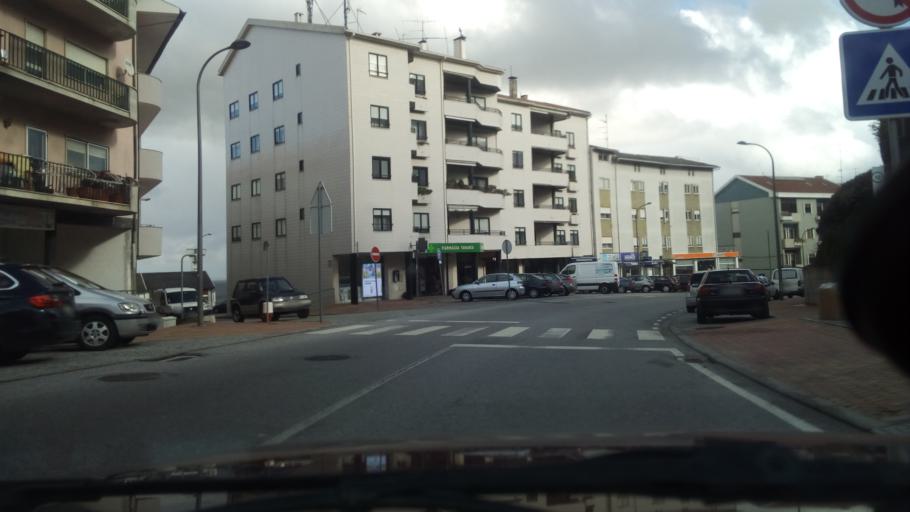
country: PT
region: Guarda
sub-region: Guarda
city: Guarda
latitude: 40.5409
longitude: -7.2624
